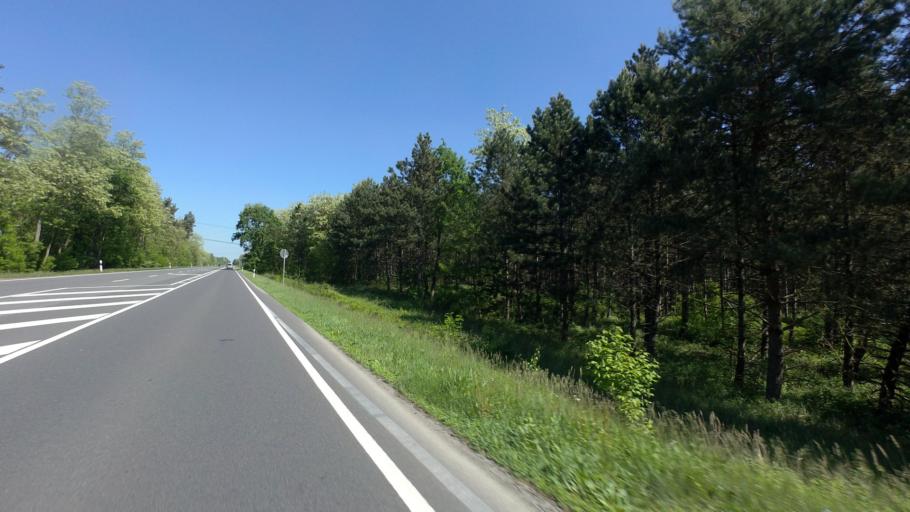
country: DE
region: Brandenburg
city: Spremberg
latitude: 51.6227
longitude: 14.3627
